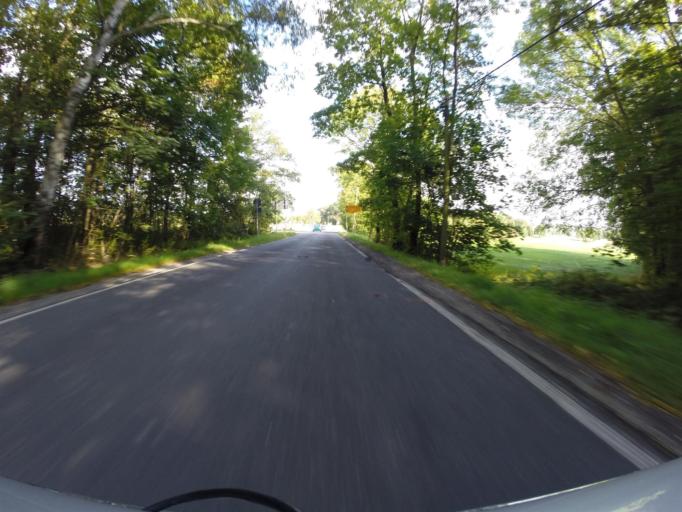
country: DE
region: Thuringia
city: Lehesten
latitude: 50.9604
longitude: 11.5653
